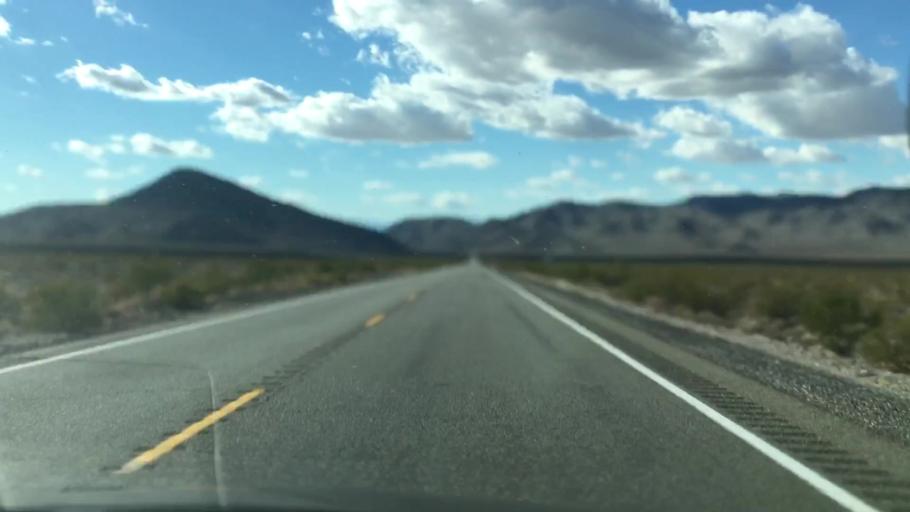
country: US
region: Nevada
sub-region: Nye County
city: Pahrump
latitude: 36.5933
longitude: -116.0227
